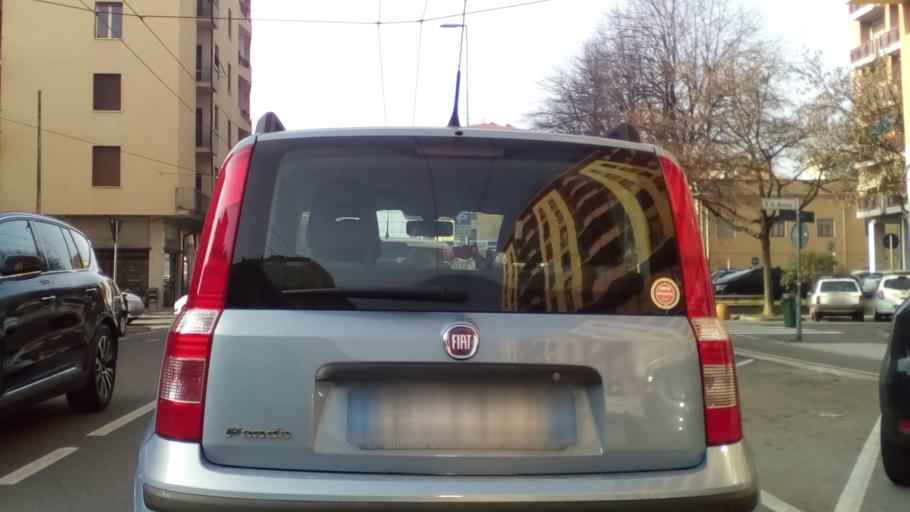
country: IT
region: Emilia-Romagna
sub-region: Provincia di Modena
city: Modena
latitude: 44.6416
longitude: 10.9375
